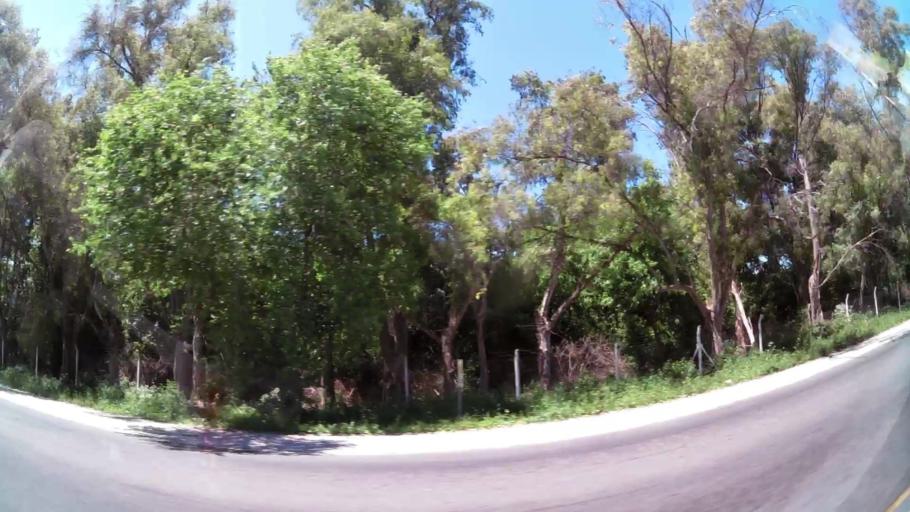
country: AR
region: Buenos Aires
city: Hurlingham
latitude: -34.5226
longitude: -58.6779
